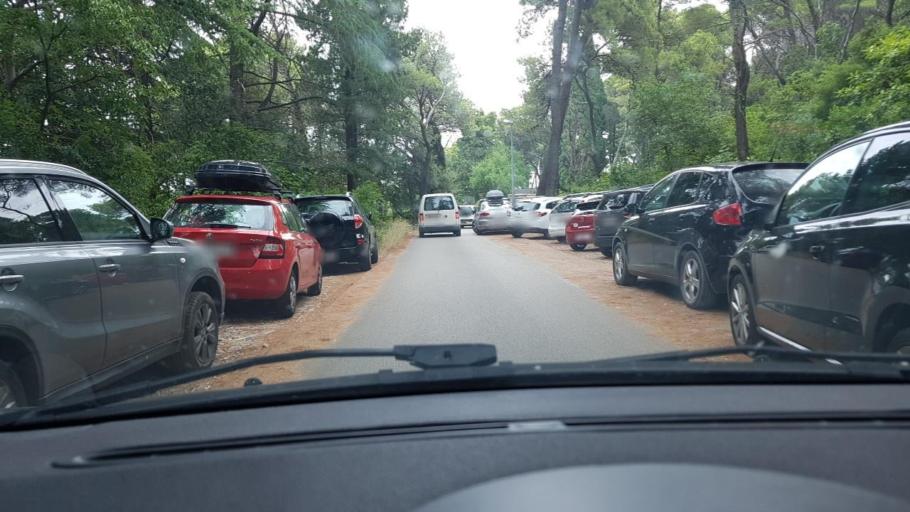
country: HR
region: Dubrovacko-Neretvanska
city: Korcula
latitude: 42.9603
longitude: 17.1300
